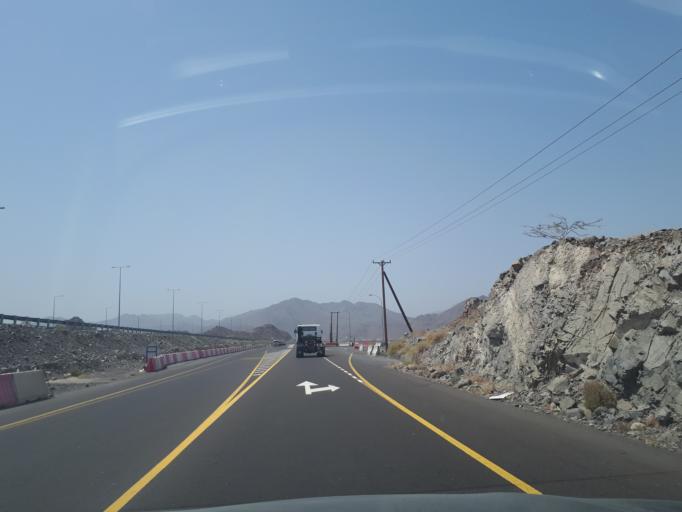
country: OM
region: Muhafazat ad Dakhiliyah
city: Sufalat Sama'il
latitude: 23.2850
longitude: 58.1081
